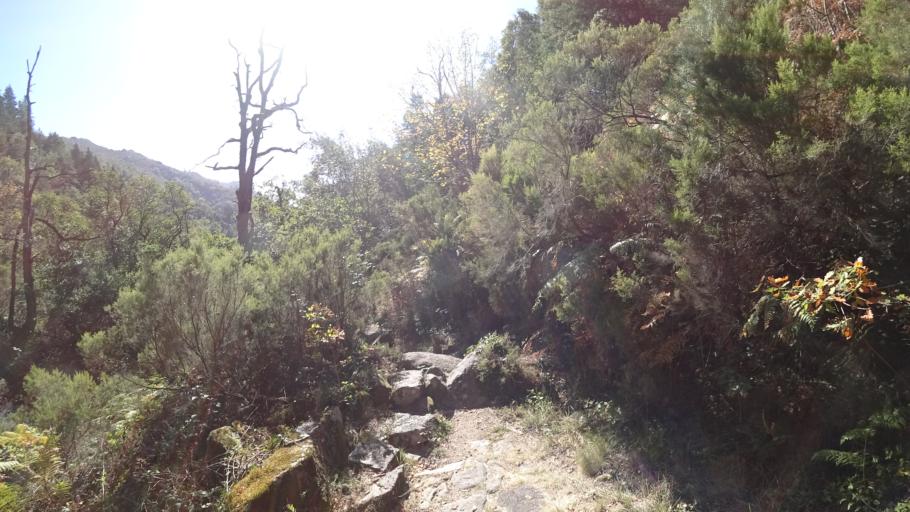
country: PT
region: Braga
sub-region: Vieira do Minho
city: Real
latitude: 41.7600
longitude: -8.1495
